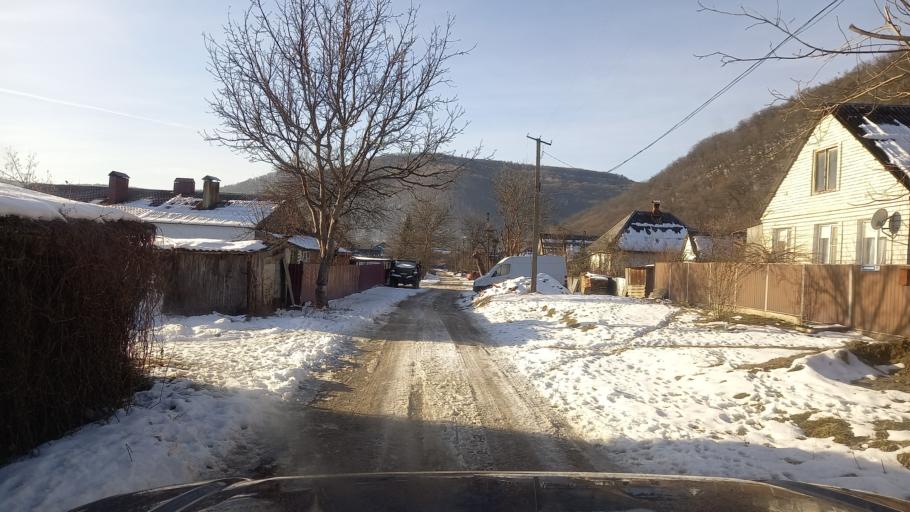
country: RU
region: Adygeya
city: Kamennomostskiy
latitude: 44.3029
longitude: 40.1692
